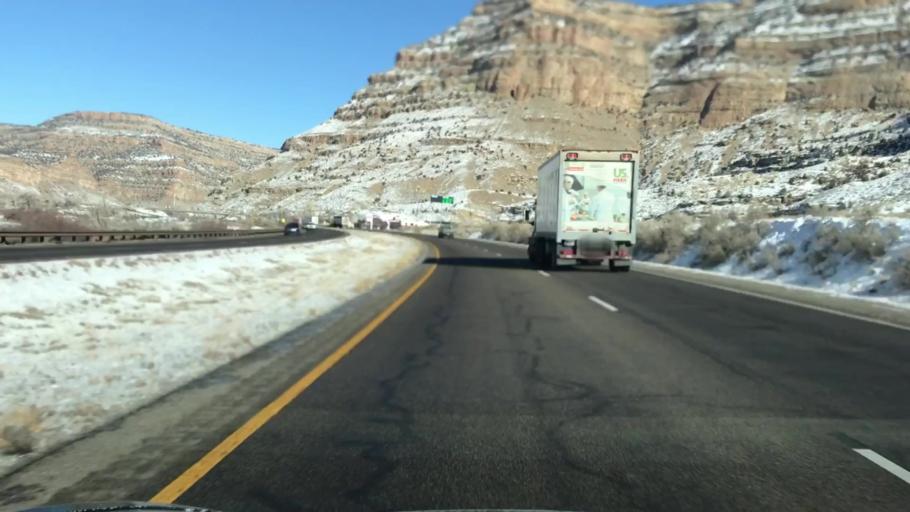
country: US
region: Colorado
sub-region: Mesa County
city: Palisade
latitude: 39.1547
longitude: -108.3012
